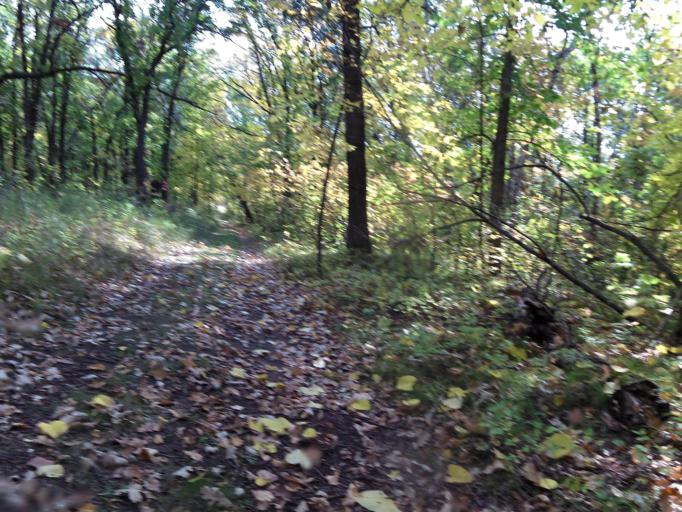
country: US
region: North Dakota
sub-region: Pembina County
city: Cavalier
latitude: 48.7802
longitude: -97.7368
